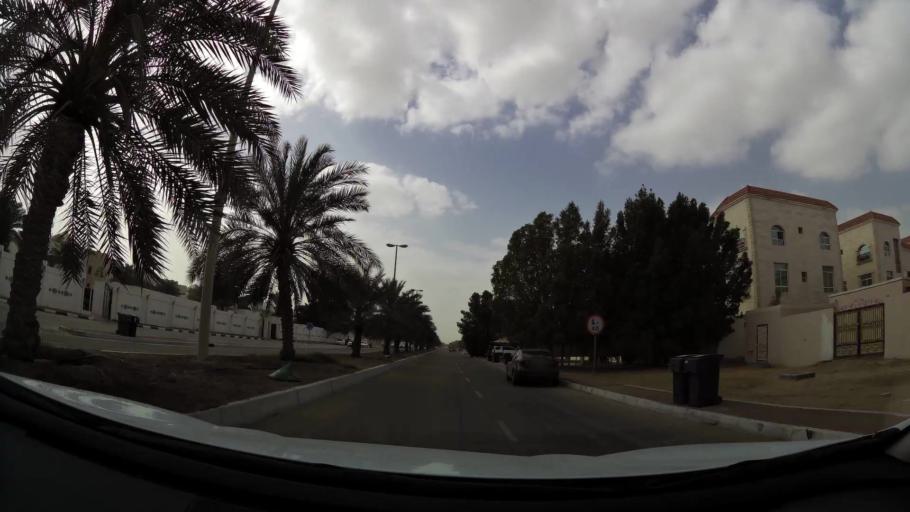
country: AE
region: Abu Dhabi
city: Abu Dhabi
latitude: 24.4100
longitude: 54.4965
